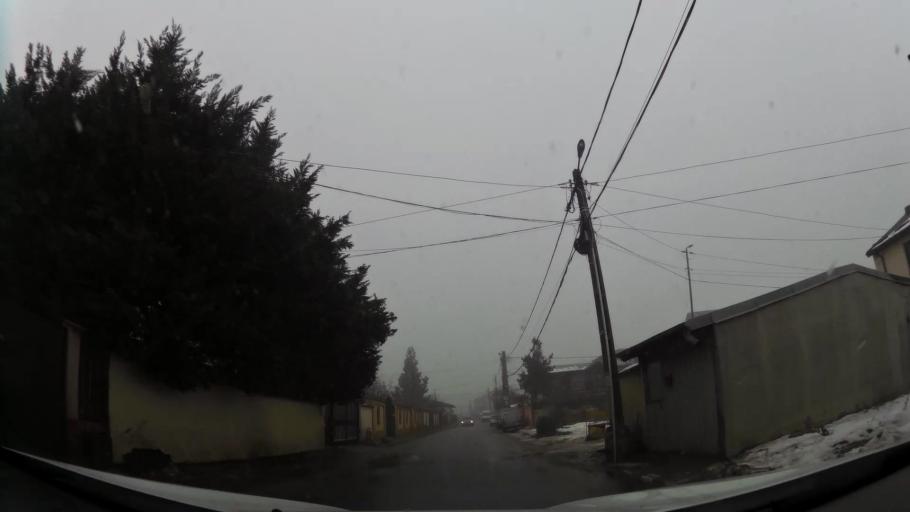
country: RO
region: Ilfov
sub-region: Comuna Chiajna
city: Chiajna
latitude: 44.4550
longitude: 25.9762
